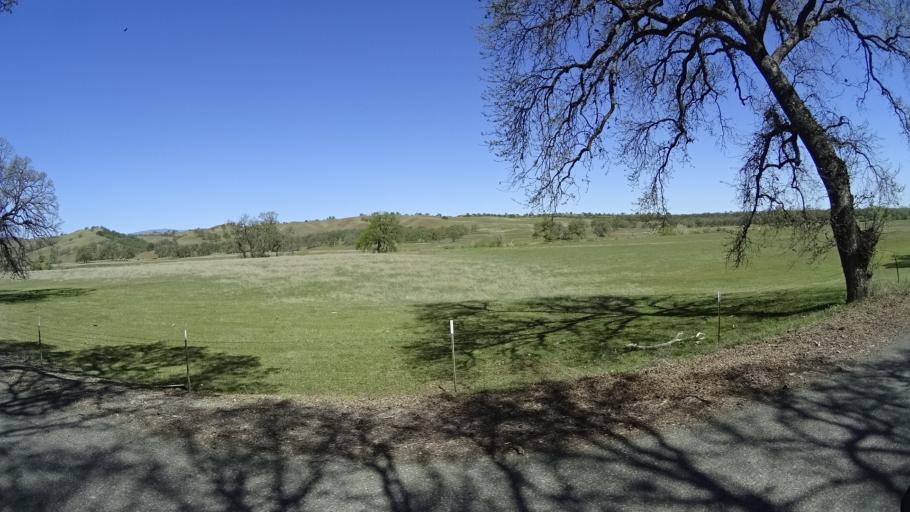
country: US
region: California
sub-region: Tehama County
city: Rancho Tehama Reserve
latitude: 39.7913
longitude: -122.4515
